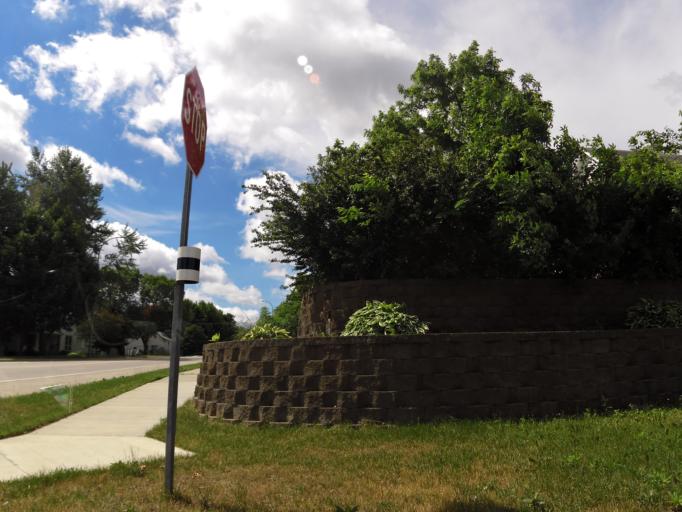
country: US
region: Minnesota
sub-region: Fillmore County
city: Spring Valley
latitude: 43.6850
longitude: -92.3893
